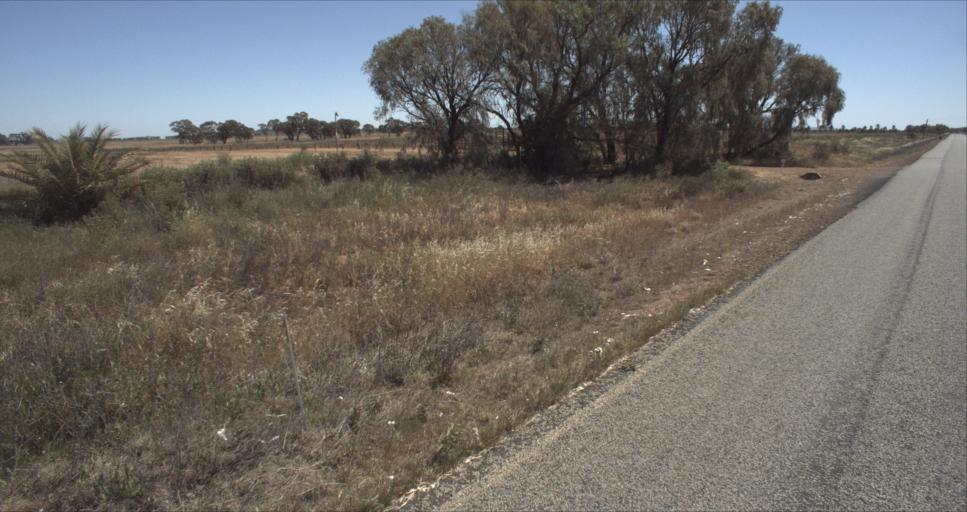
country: AU
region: New South Wales
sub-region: Leeton
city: Leeton
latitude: -34.4493
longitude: 146.2963
